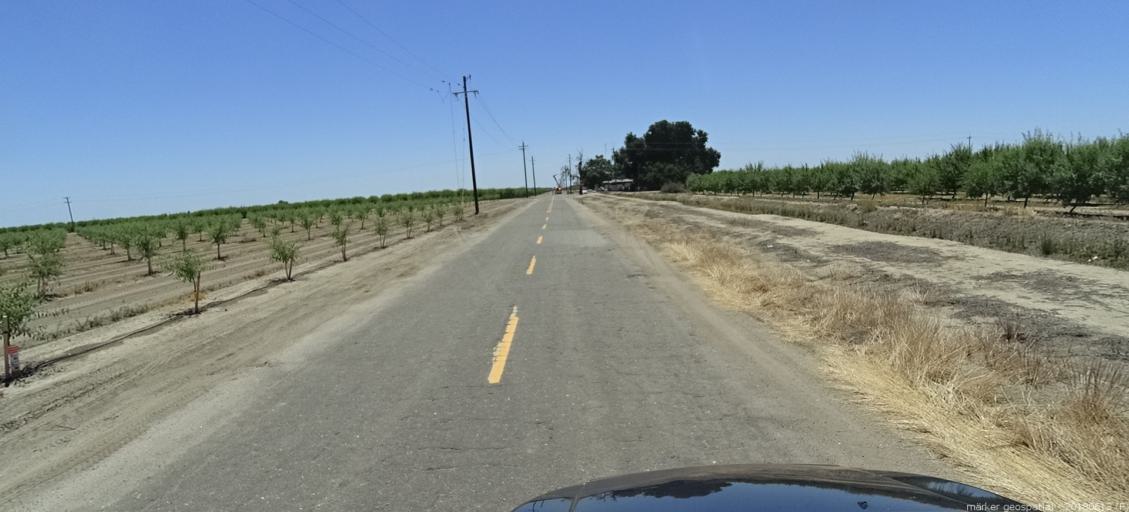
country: US
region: California
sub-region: Madera County
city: Chowchilla
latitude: 37.0413
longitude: -120.2744
